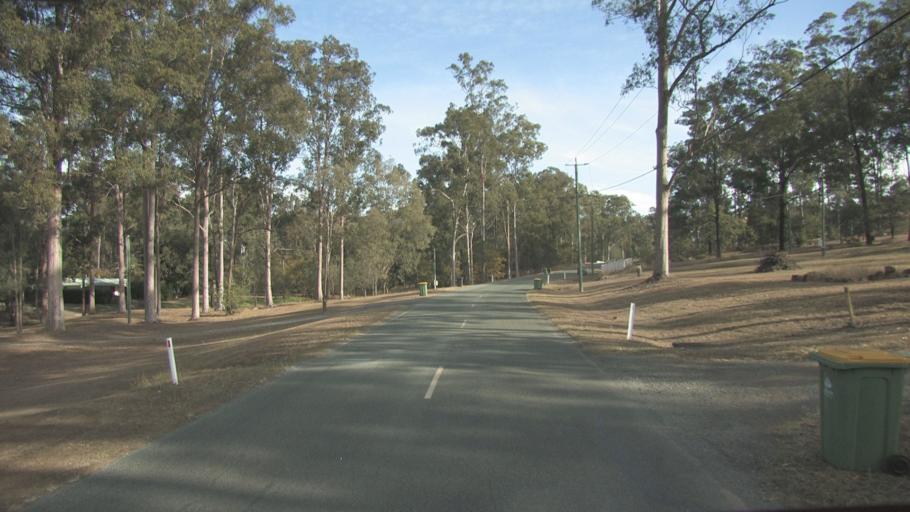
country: AU
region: Queensland
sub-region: Logan
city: Cedar Vale
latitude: -27.8792
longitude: 153.0005
